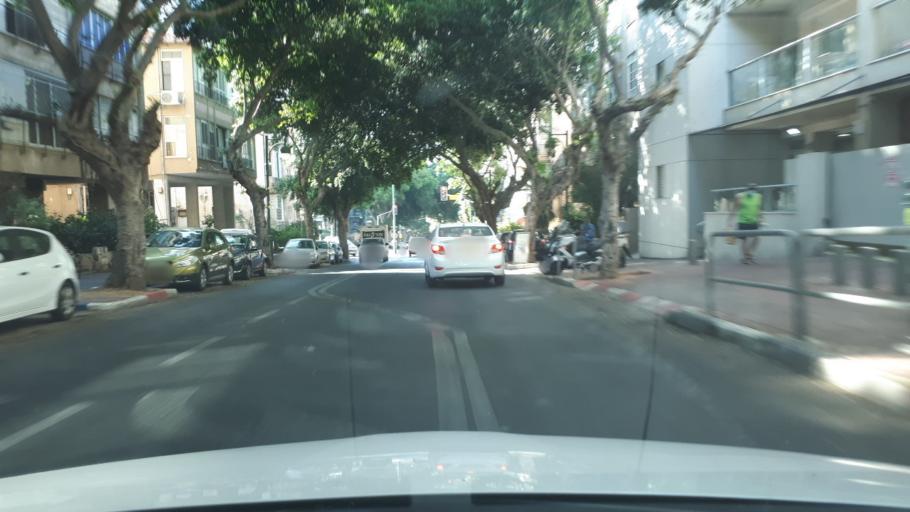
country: IL
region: Tel Aviv
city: Ramat Gan
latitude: 32.0806
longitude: 34.8195
